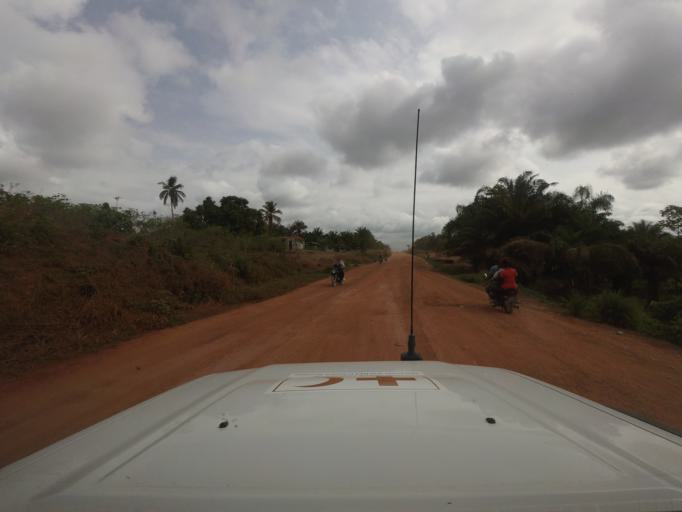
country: LR
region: Bong
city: Gbarnga
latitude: 7.0123
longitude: -9.4777
